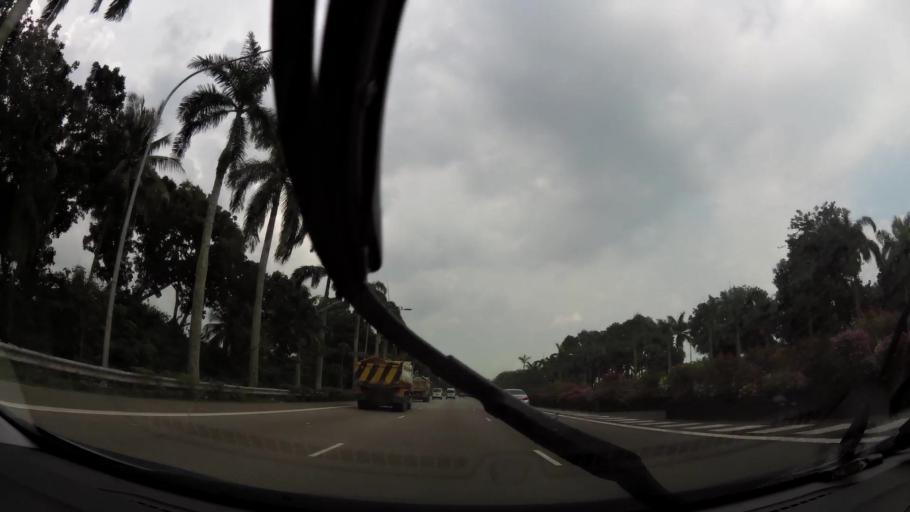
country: SG
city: Singapore
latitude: 1.3174
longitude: 103.9640
